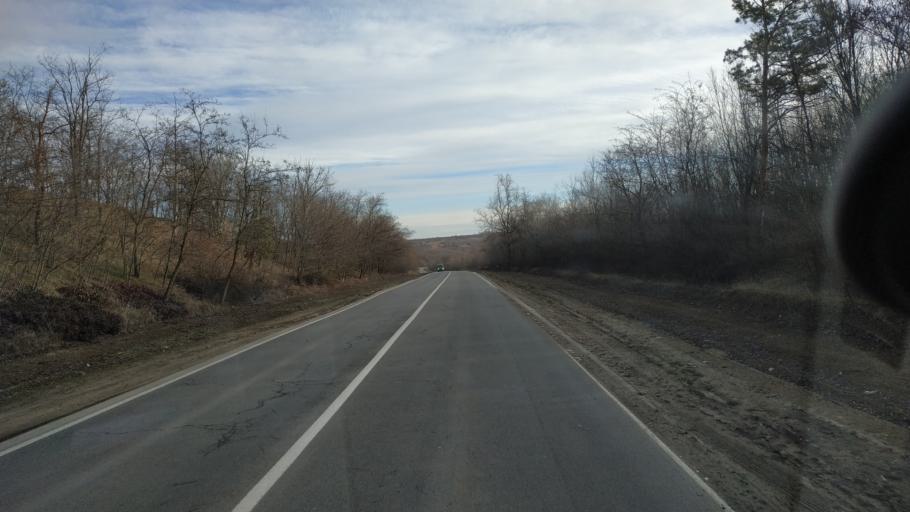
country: MD
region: Chisinau
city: Vadul lui Voda
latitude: 47.0788
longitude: 29.0311
